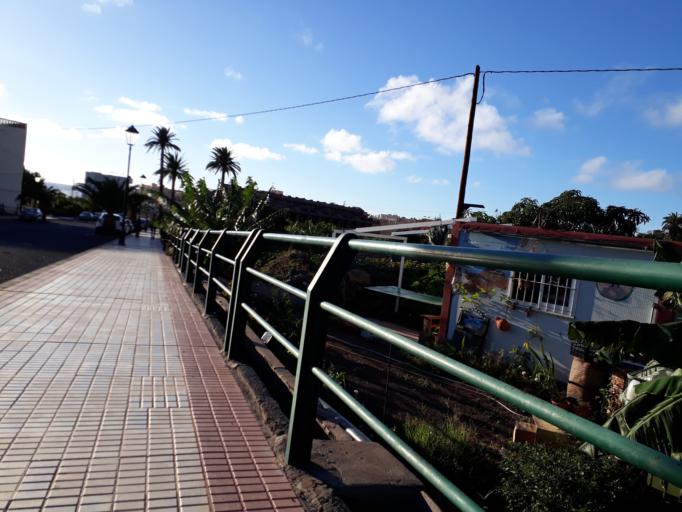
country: ES
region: Canary Islands
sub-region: Provincia de Santa Cruz de Tenerife
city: Alajero
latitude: 28.0949
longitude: -17.3401
